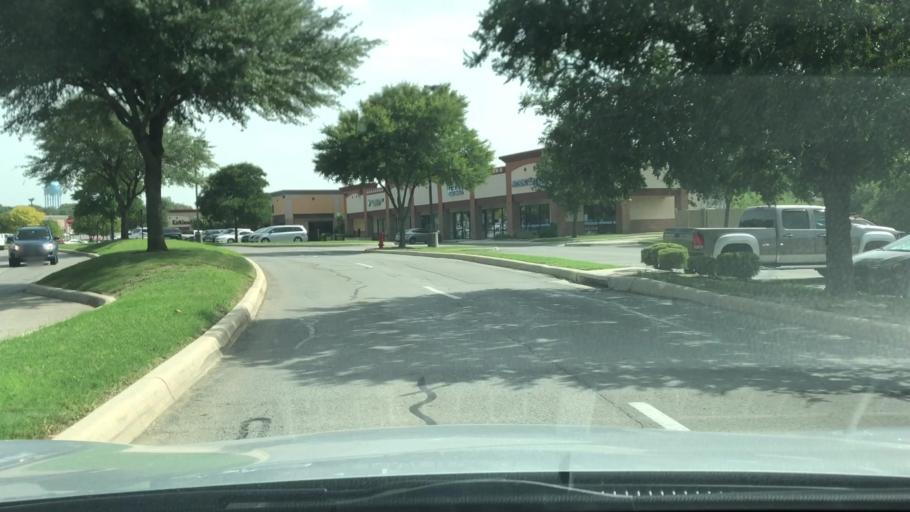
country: US
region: Texas
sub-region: Bexar County
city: Live Oak
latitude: 29.5740
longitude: -98.3241
